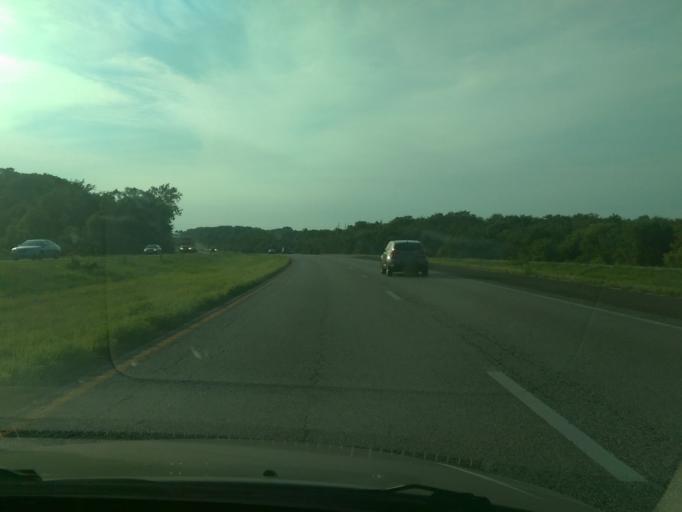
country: US
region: Missouri
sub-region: Platte County
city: Weatherby Lake
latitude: 39.3204
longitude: -94.6960
